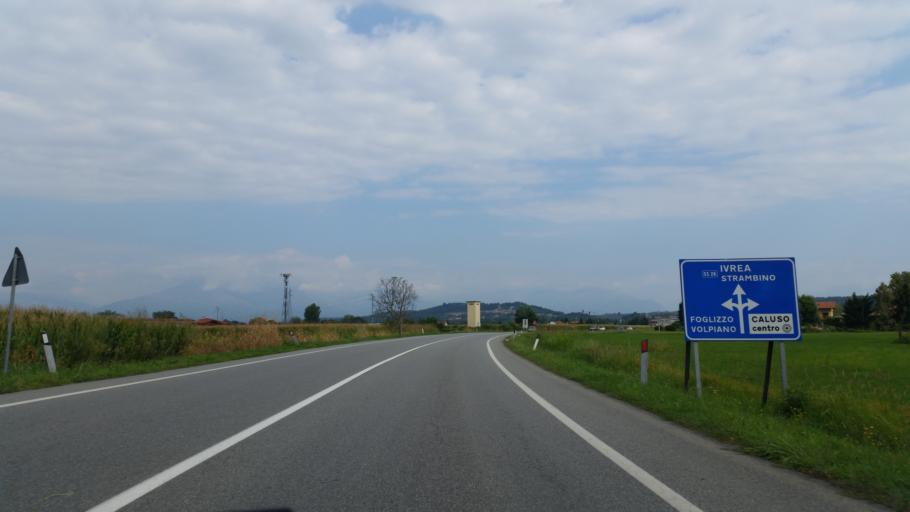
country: IT
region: Piedmont
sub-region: Provincia di Torino
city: Caluso
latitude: 45.2997
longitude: 7.8798
